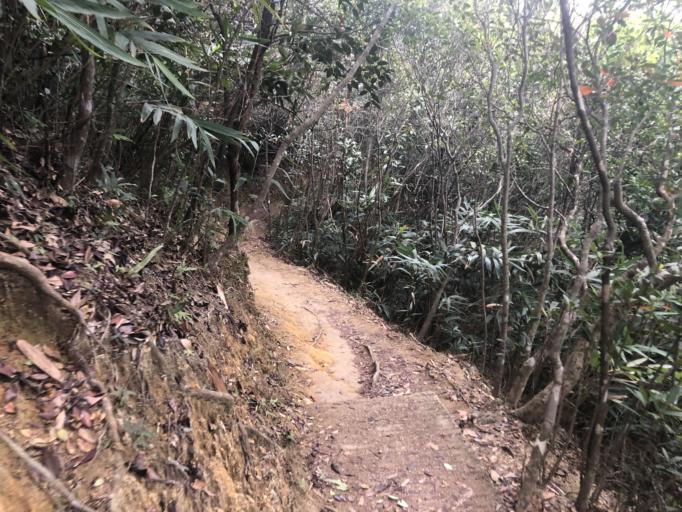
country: HK
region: Wanchai
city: Wan Chai
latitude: 22.2774
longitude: 114.2111
